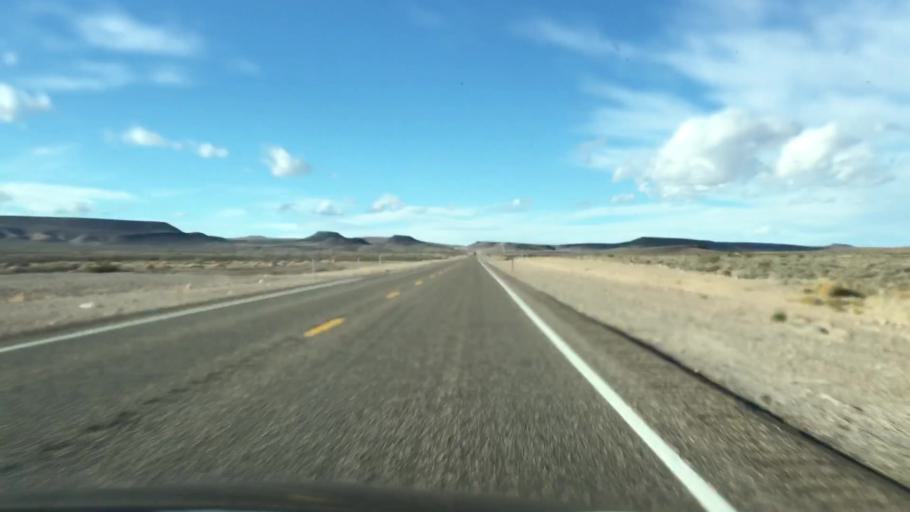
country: US
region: Nevada
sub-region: Esmeralda County
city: Goldfield
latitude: 37.3563
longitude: -117.1116
